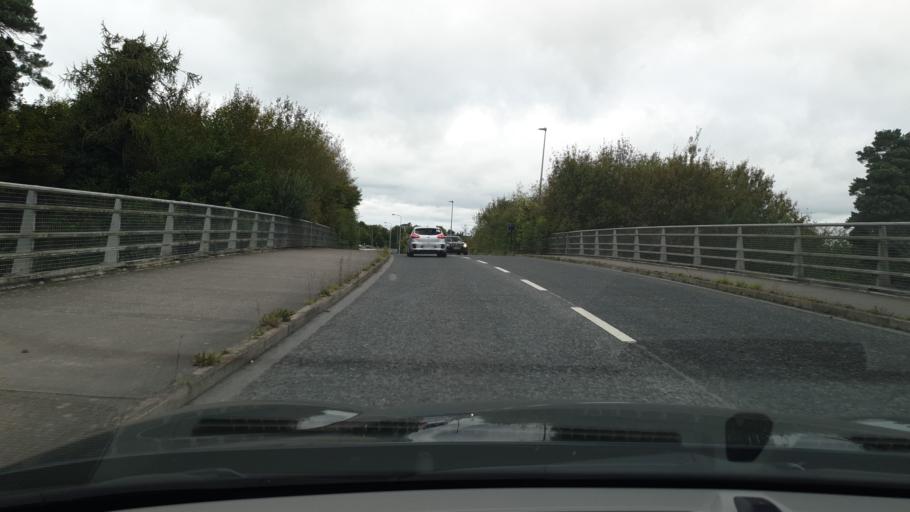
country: IE
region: Leinster
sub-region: Kildare
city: Naas
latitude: 53.2163
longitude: -6.6789
